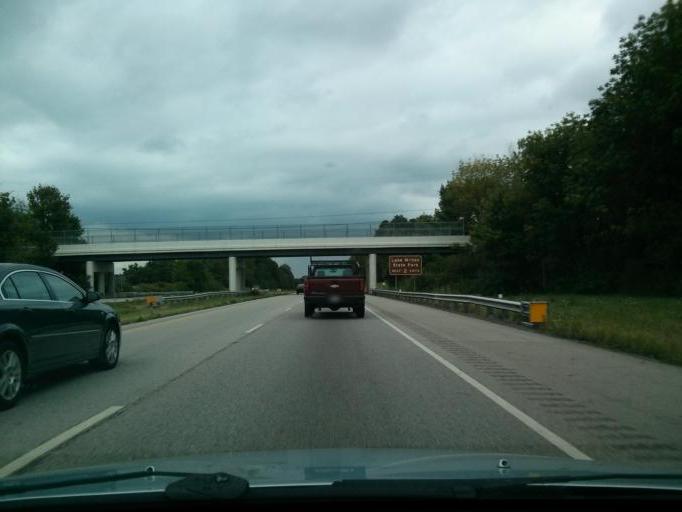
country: US
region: Ohio
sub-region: Mahoning County
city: Craig Beach
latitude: 41.1059
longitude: -81.0715
